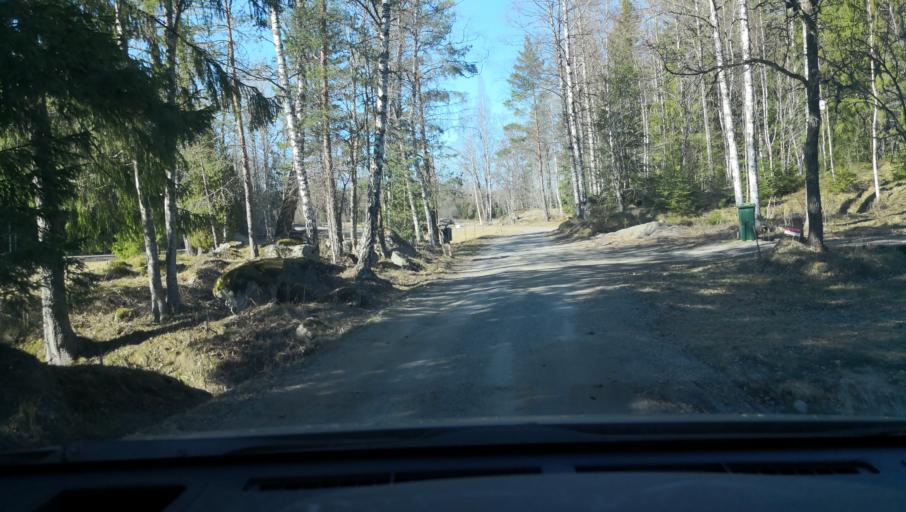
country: SE
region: Vaestmanland
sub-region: Sala Kommun
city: Sala
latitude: 59.9435
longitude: 16.4387
